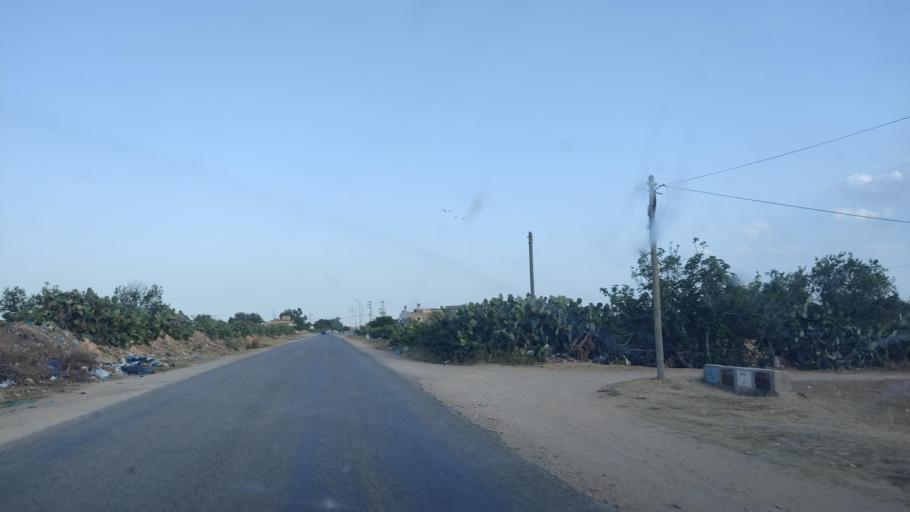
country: TN
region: Safaqis
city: Sfax
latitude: 34.8109
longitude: 10.6621
